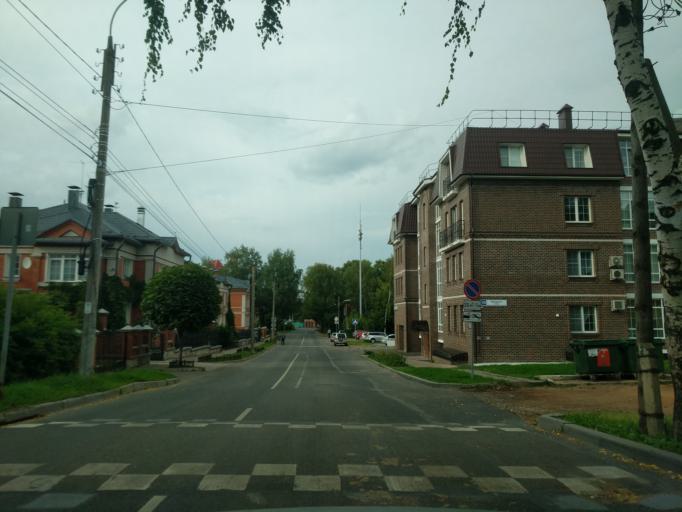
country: RU
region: Kirov
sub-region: Kirovo-Chepetskiy Rayon
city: Kirov
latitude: 58.5978
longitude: 49.6881
